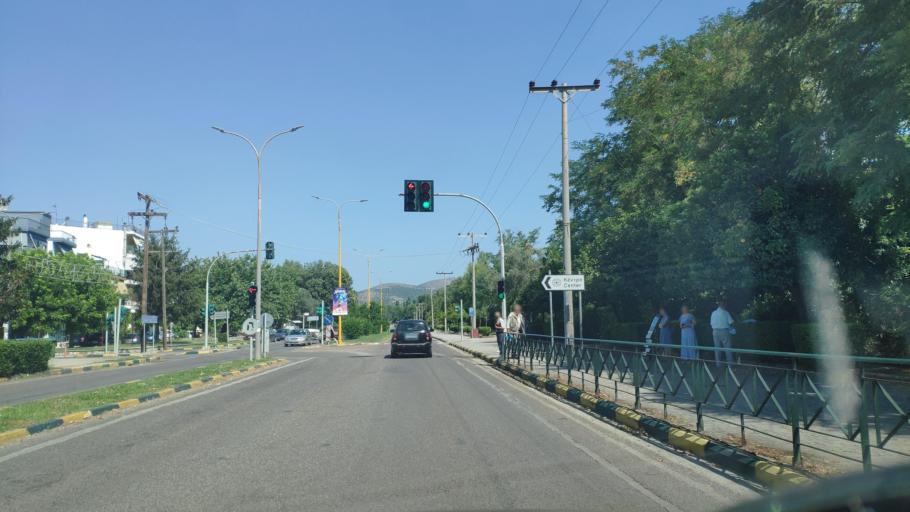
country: GR
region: Epirus
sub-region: Nomos Artas
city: Arta
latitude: 39.1631
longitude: 20.9922
